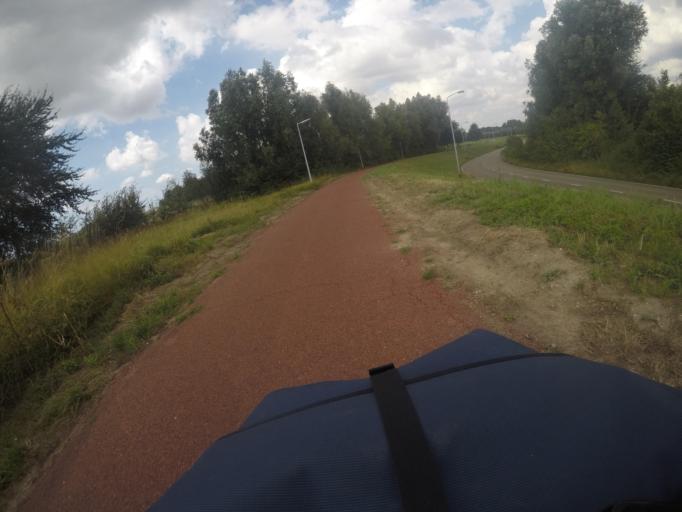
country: NL
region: North Holland
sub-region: Gemeente Amstelveen
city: Amstelveen
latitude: 52.3272
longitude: 4.8003
